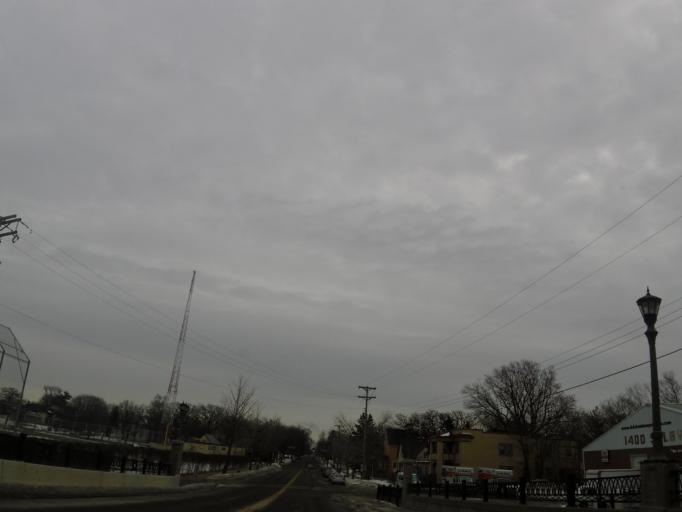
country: US
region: Minnesota
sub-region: Ramsey County
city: Falcon Heights
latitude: 44.9466
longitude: -93.1592
